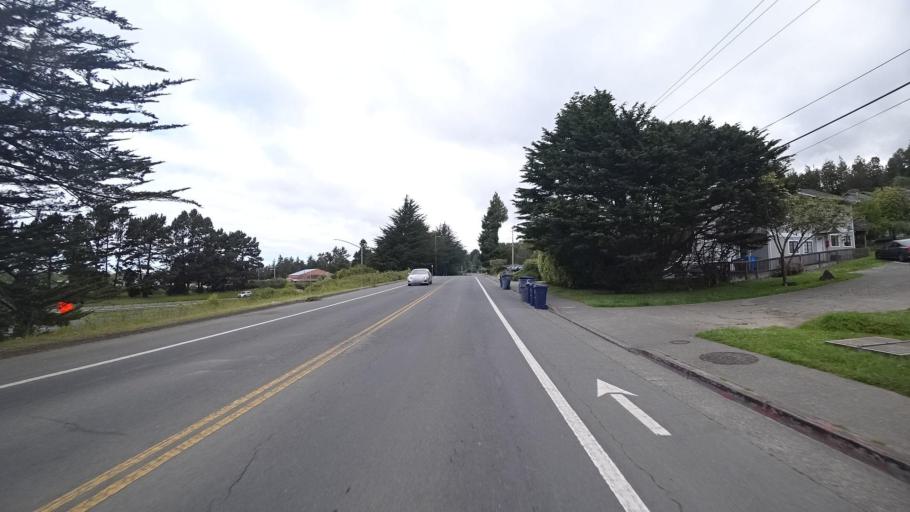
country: US
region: California
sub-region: Humboldt County
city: Arcata
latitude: 40.8835
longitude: -124.0802
